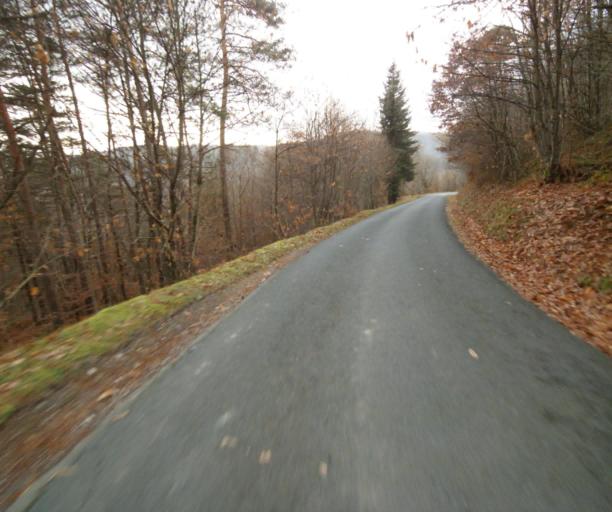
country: FR
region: Limousin
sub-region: Departement de la Correze
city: Chameyrat
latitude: 45.2271
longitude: 1.7040
